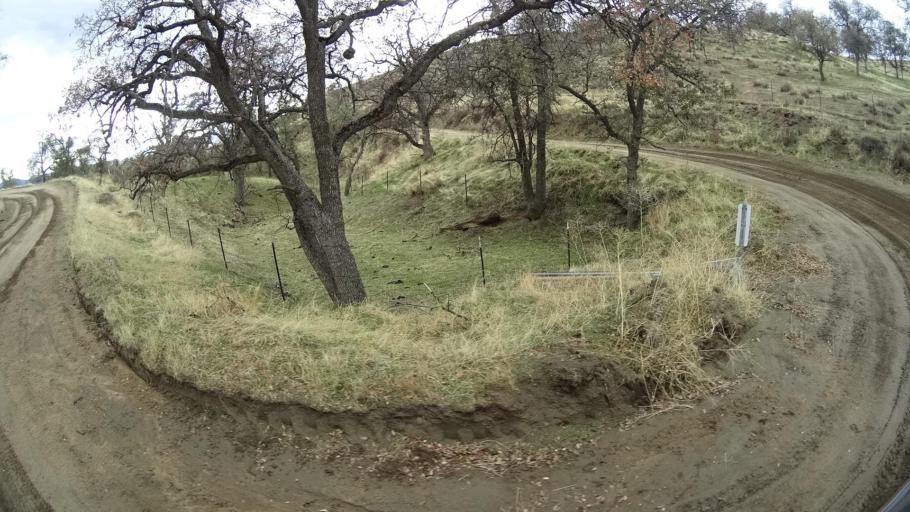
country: US
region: California
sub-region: Kern County
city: Stallion Springs
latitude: 35.1254
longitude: -118.7276
